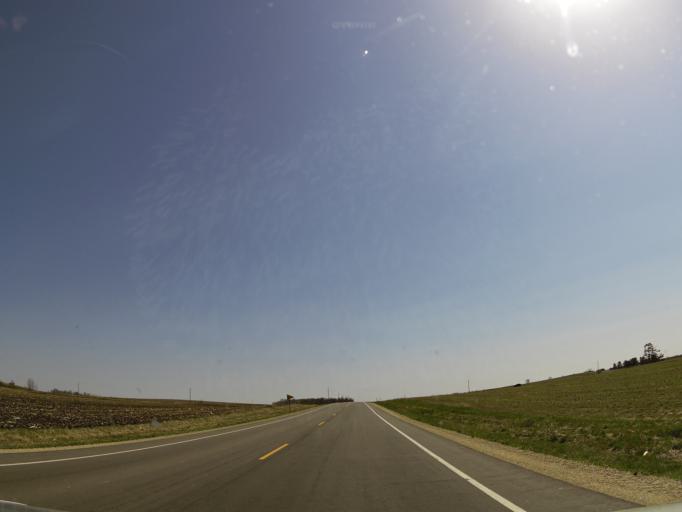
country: US
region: Wisconsin
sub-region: Saint Croix County
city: Hammond
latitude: 44.8904
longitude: -92.4355
